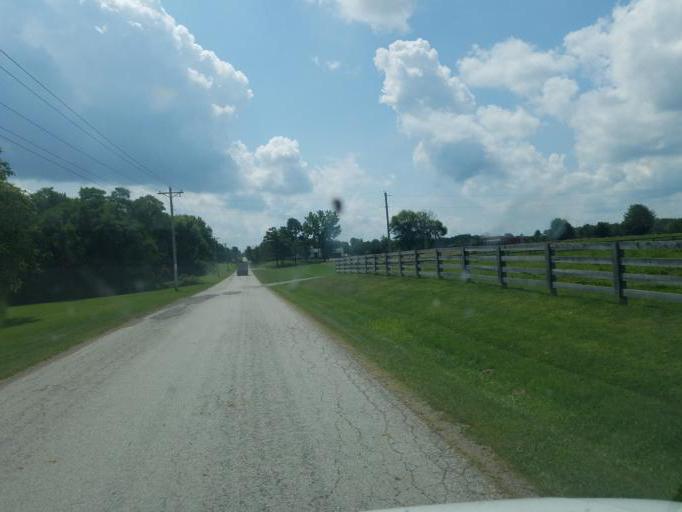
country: US
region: Ohio
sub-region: Knox County
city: Centerburg
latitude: 40.3951
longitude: -82.6525
